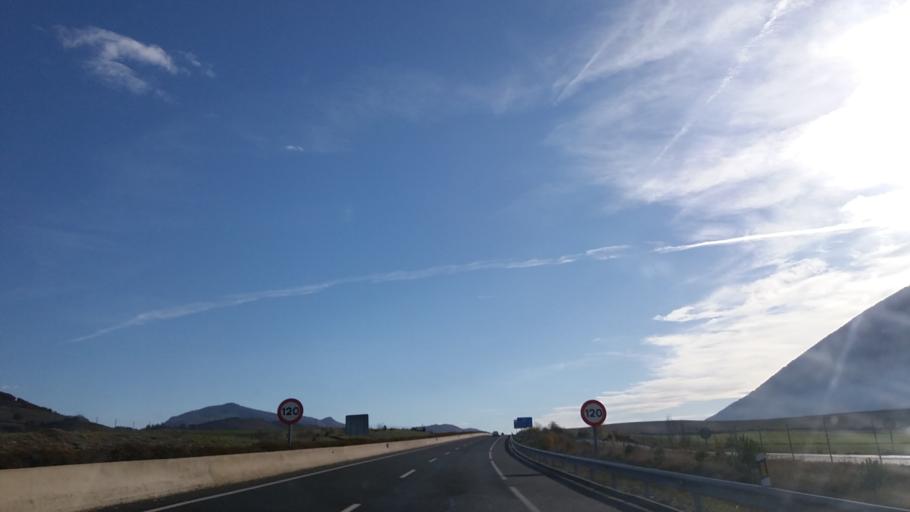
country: ES
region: Navarre
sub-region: Provincia de Navarra
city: Elorz
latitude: 42.7279
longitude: -1.5545
